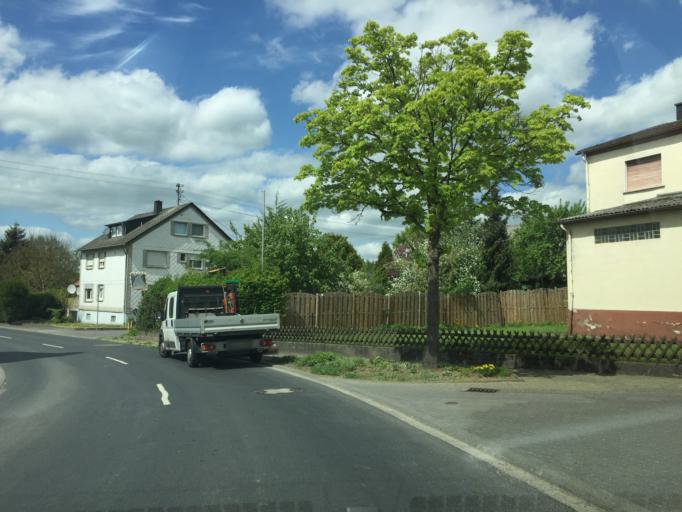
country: DE
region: Rheinland-Pfalz
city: Berod bei Wallmerod
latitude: 50.4814
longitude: 7.9346
